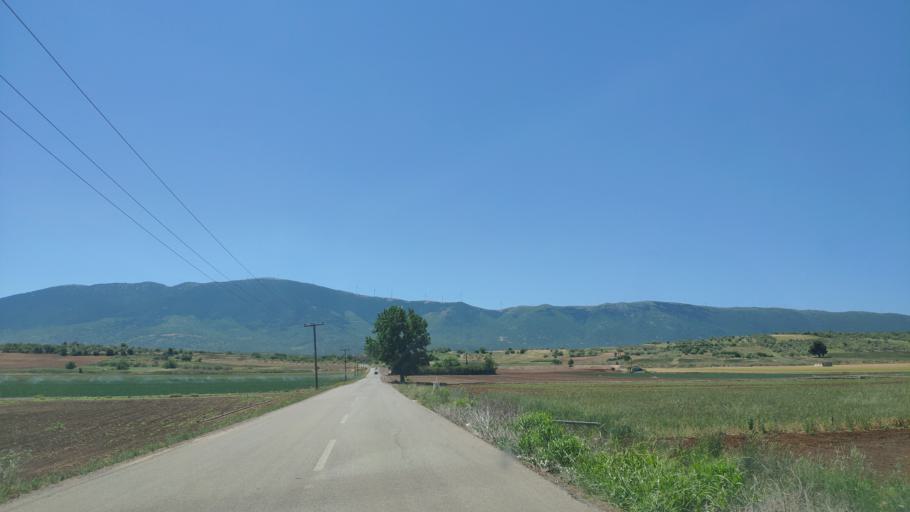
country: GR
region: Central Greece
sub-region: Nomos Voiotias
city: Kaparellion
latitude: 38.2565
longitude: 23.2352
